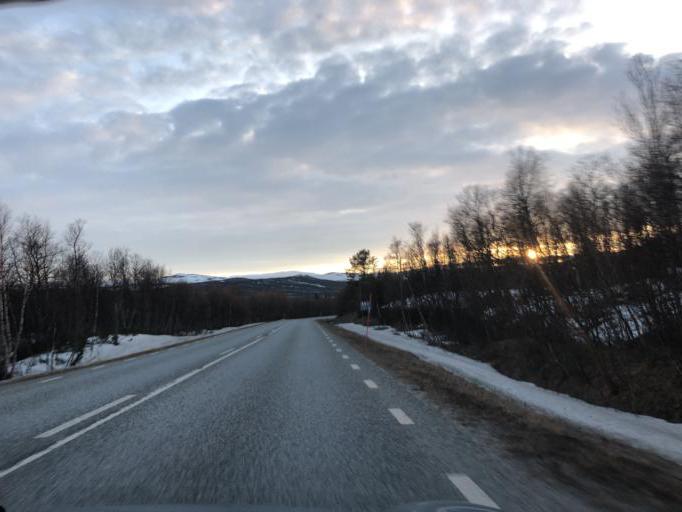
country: NO
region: Hedmark
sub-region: Engerdal
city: Engerdal
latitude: 62.5347
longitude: 12.3681
